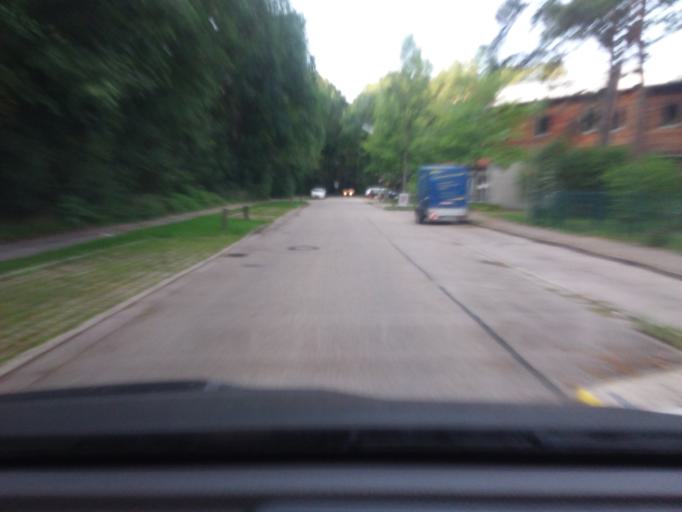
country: DE
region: Bavaria
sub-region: Upper Bavaria
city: Oberschleissheim
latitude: 48.2553
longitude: 11.5647
